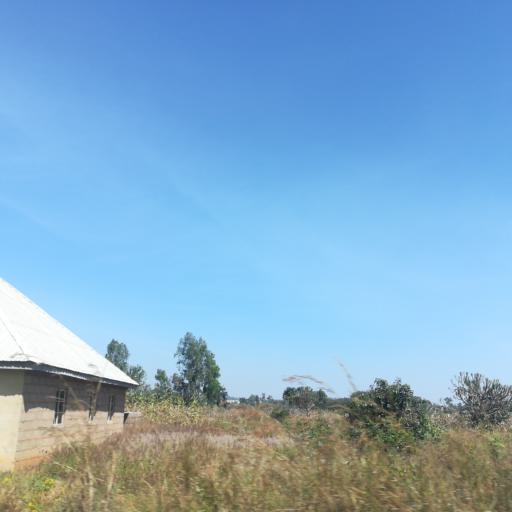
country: NG
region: Plateau
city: Bukuru
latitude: 9.7572
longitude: 8.8719
